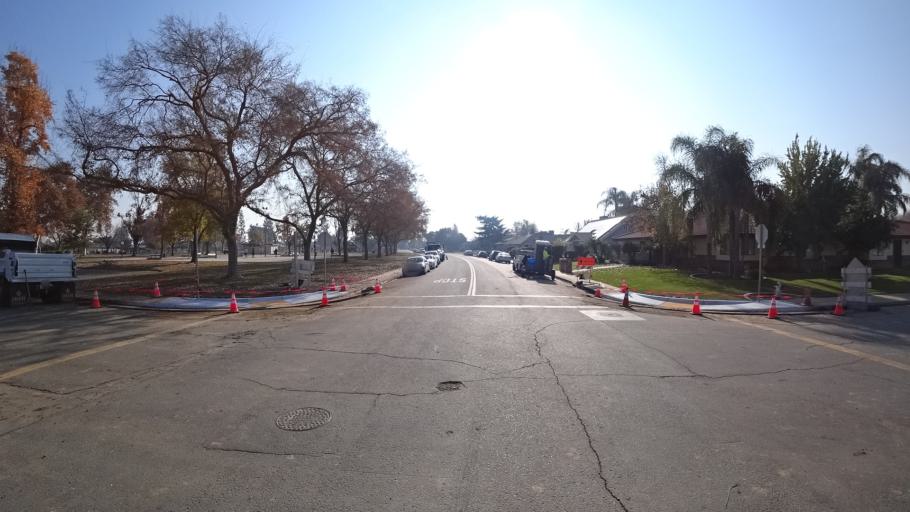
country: US
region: California
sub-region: Kern County
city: Bakersfield
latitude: 35.3617
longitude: -119.0543
